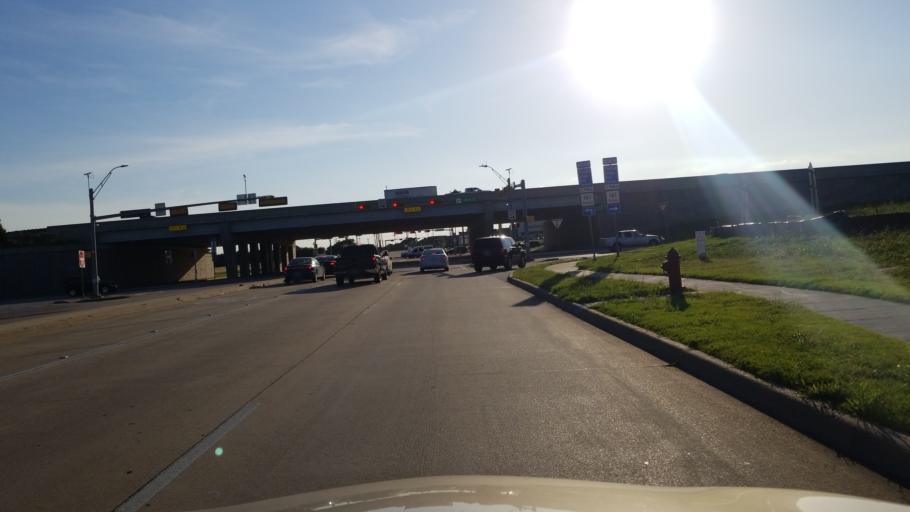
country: US
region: Texas
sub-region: Dallas County
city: Grand Prairie
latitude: 32.6918
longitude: -97.0232
